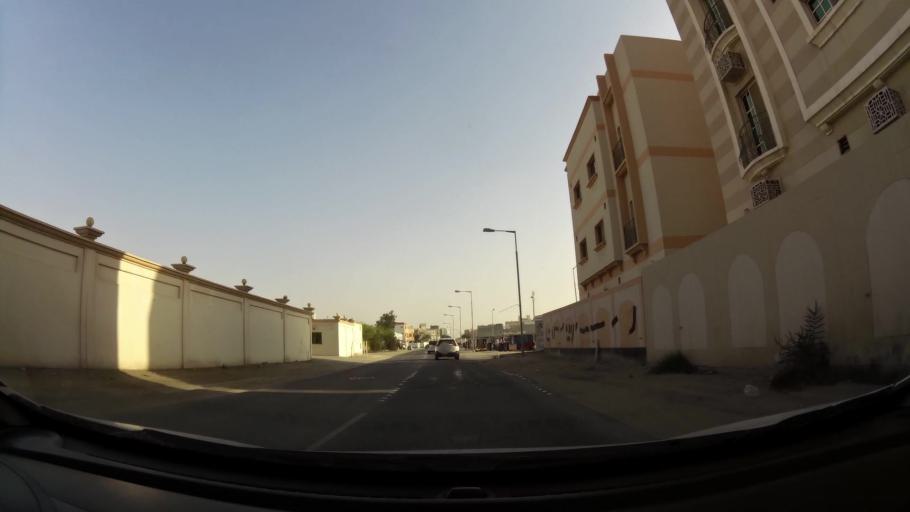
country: BH
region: Manama
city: Jidd Hafs
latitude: 26.2182
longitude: 50.4991
